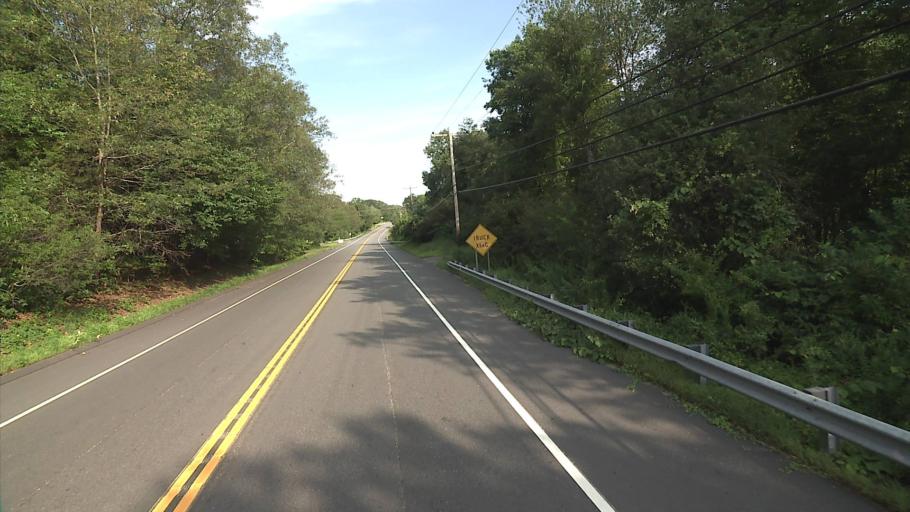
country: US
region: Connecticut
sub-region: New London County
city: Norwich
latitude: 41.5021
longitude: -72.0364
